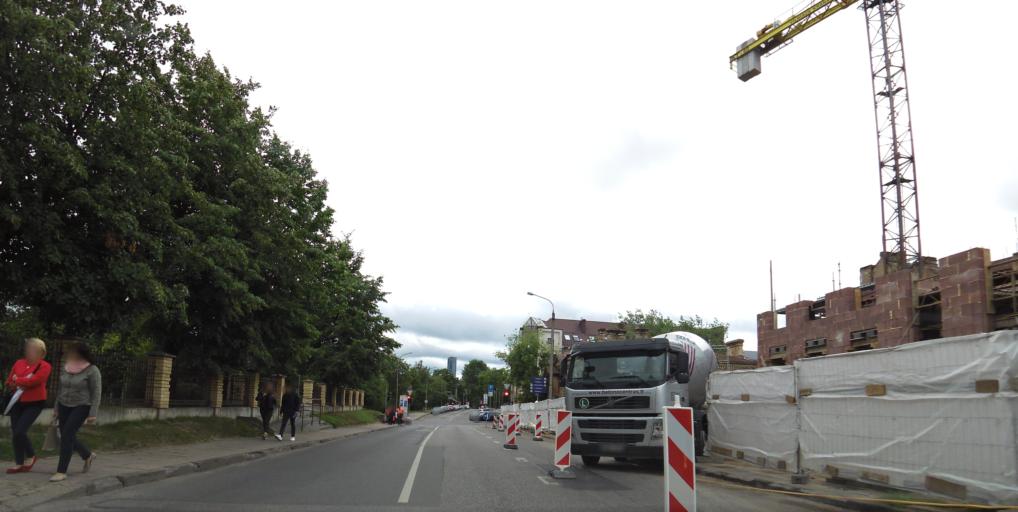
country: LT
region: Vilnius County
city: Naujamiestis
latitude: 54.6910
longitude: 25.2564
